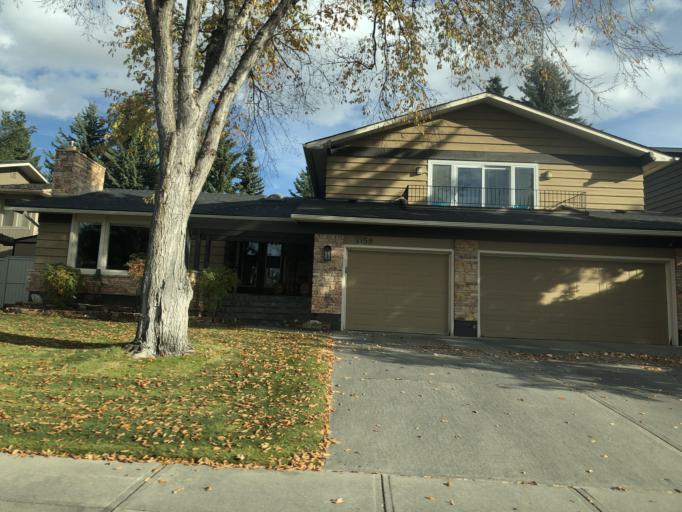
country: CA
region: Alberta
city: Calgary
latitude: 50.9361
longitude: -114.0596
